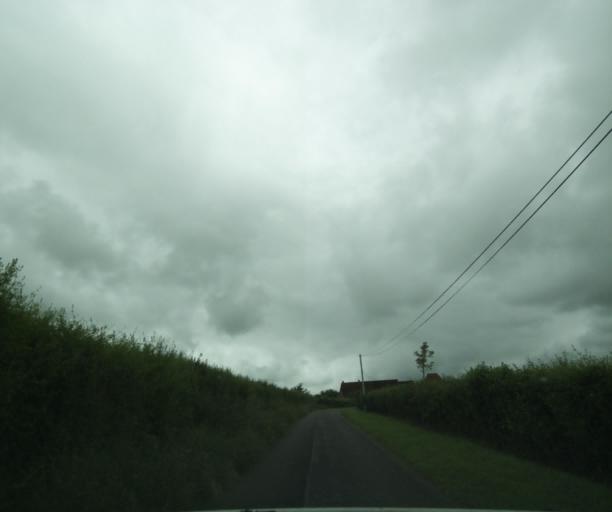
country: FR
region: Bourgogne
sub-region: Departement de Saone-et-Loire
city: Charolles
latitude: 46.4797
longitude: 4.3237
